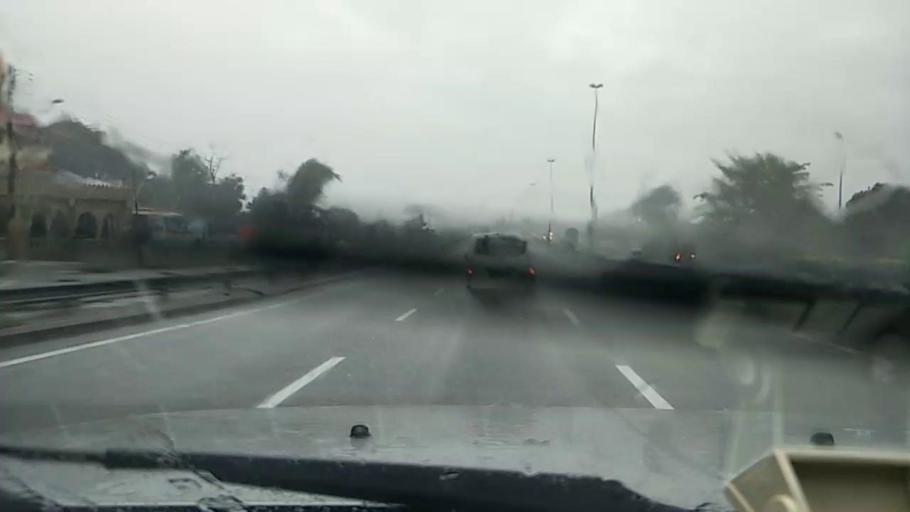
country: MY
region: Selangor
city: Kampong Baharu Balakong
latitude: 2.9840
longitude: 101.7643
